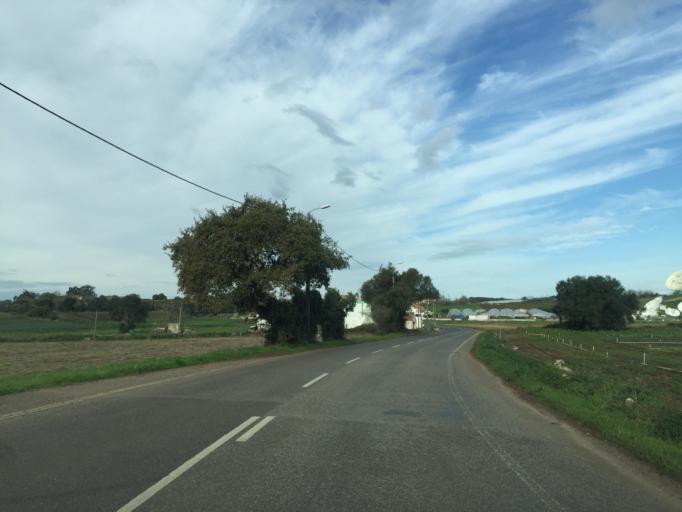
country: PT
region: Lisbon
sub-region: Sintra
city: Almargem
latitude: 38.8646
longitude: -9.2819
